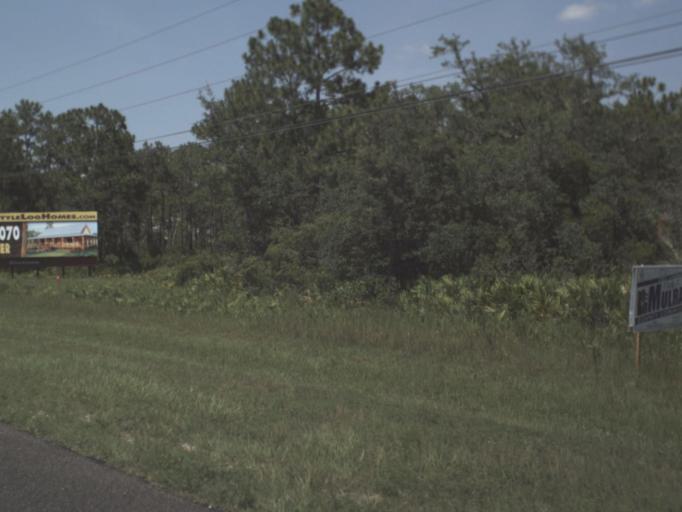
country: US
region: Florida
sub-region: Citrus County
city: Homosassa Springs
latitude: 28.7578
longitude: -82.5529
